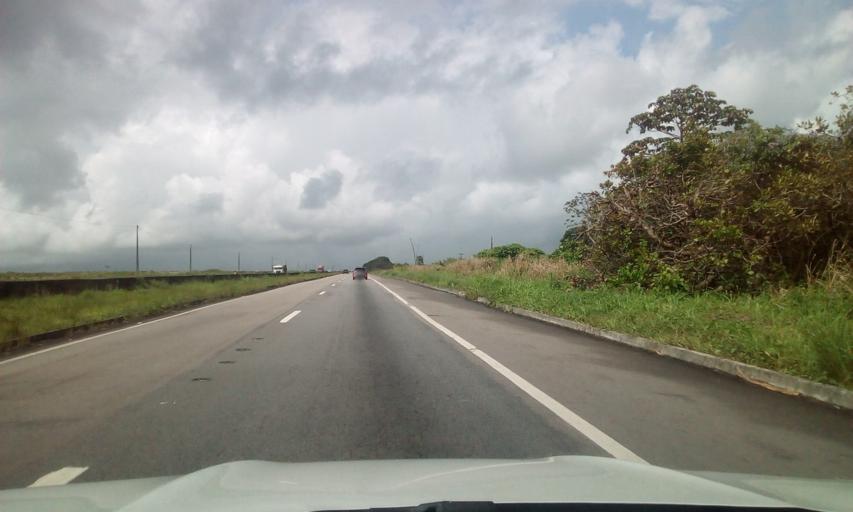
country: BR
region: Paraiba
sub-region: Alhandra
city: Alhandra
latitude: -7.4729
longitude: -34.9777
